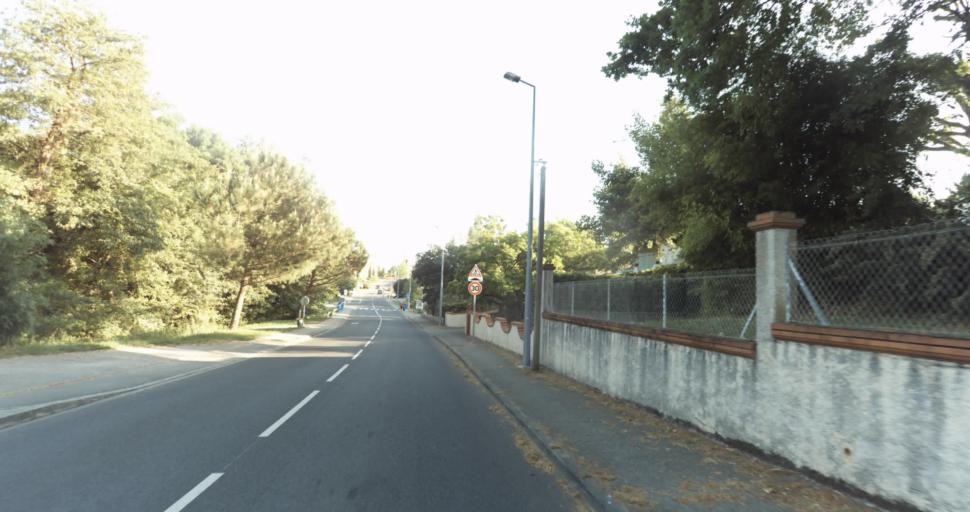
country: FR
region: Midi-Pyrenees
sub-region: Departement de la Haute-Garonne
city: Leguevin
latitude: 43.5961
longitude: 1.2349
